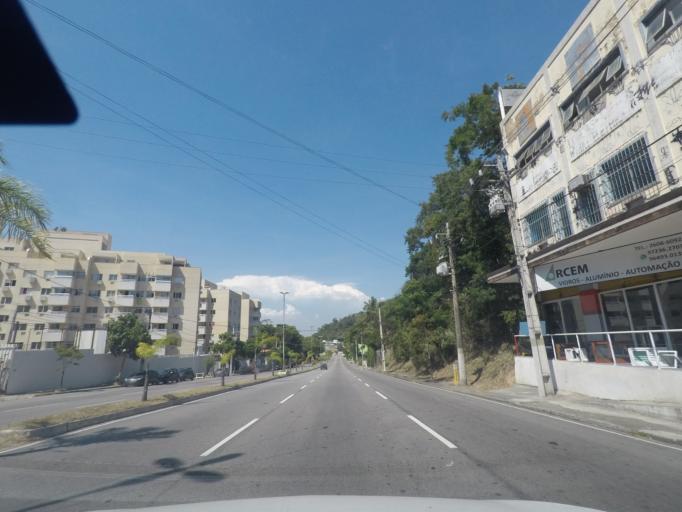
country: BR
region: Rio de Janeiro
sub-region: Niteroi
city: Niteroi
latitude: -22.9190
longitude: -43.0518
